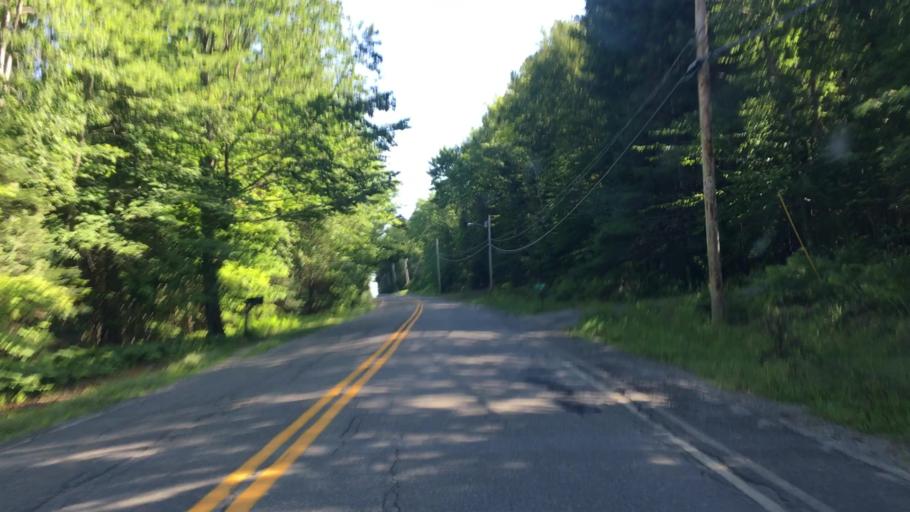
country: US
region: Maine
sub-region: Penobscot County
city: Enfield
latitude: 45.2696
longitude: -68.5615
